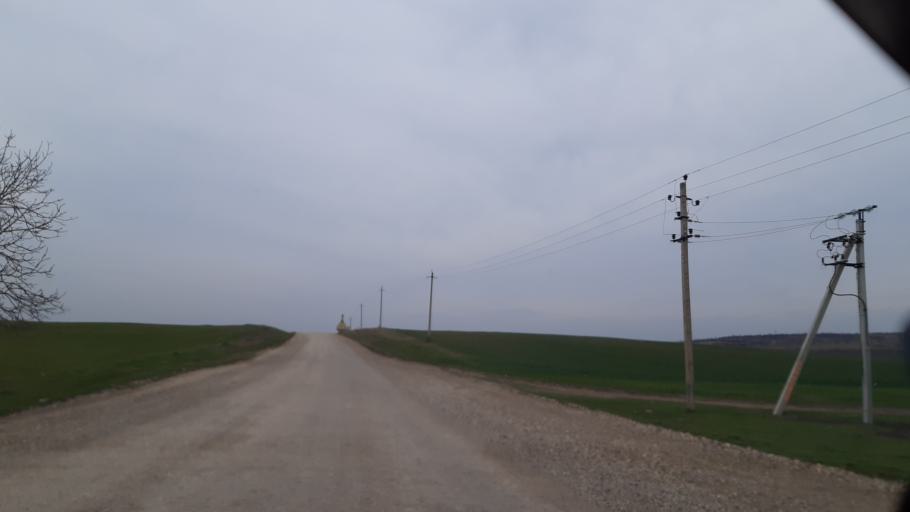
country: MD
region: Soldanesti
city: Soldanesti
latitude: 47.6213
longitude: 28.6585
